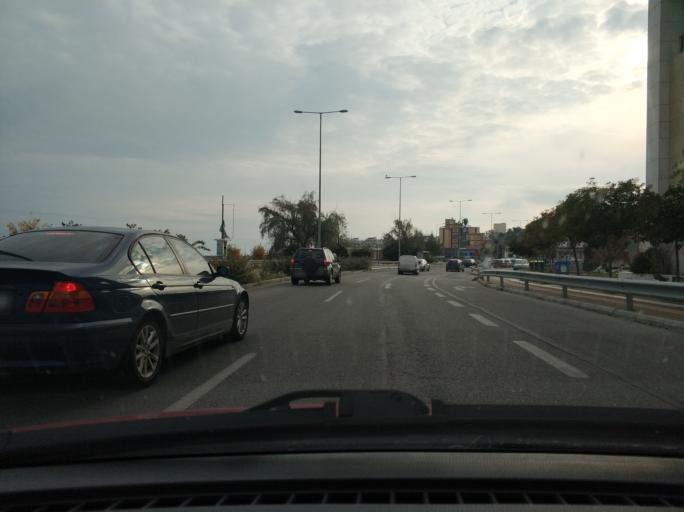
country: GR
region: East Macedonia and Thrace
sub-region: Nomos Kavalas
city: Kavala
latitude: 40.9301
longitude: 24.3915
